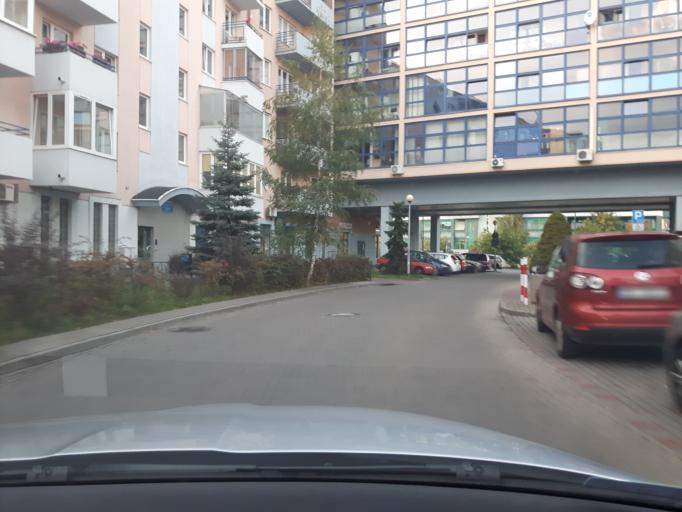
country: PL
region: Masovian Voivodeship
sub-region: Warszawa
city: Kabaty
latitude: 52.1305
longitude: 21.0647
